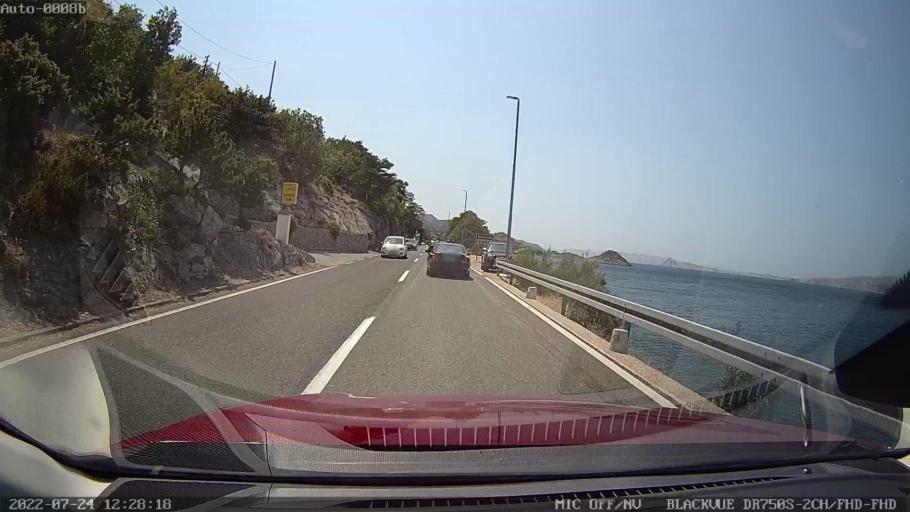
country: HR
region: Licko-Senjska
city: Senj
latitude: 44.9382
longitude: 14.9221
